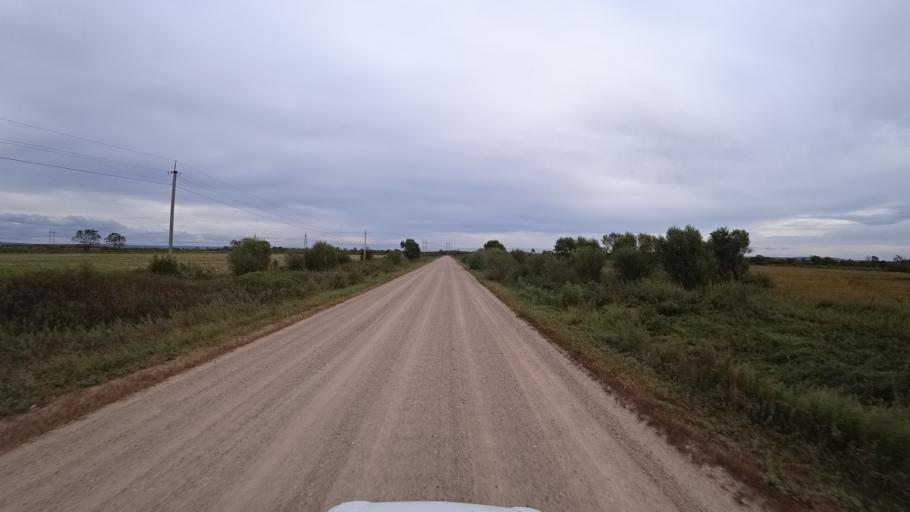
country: RU
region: Amur
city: Arkhara
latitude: 49.4304
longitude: 130.2403
